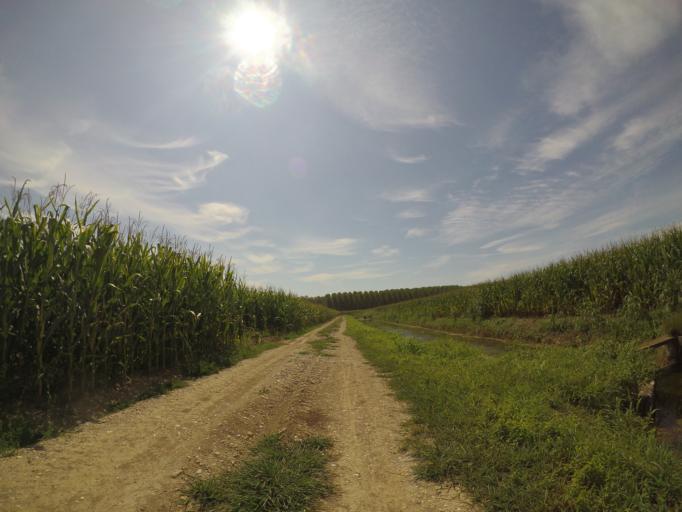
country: IT
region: Friuli Venezia Giulia
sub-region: Provincia di Udine
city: Varmo
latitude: 45.9192
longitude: 13.0179
